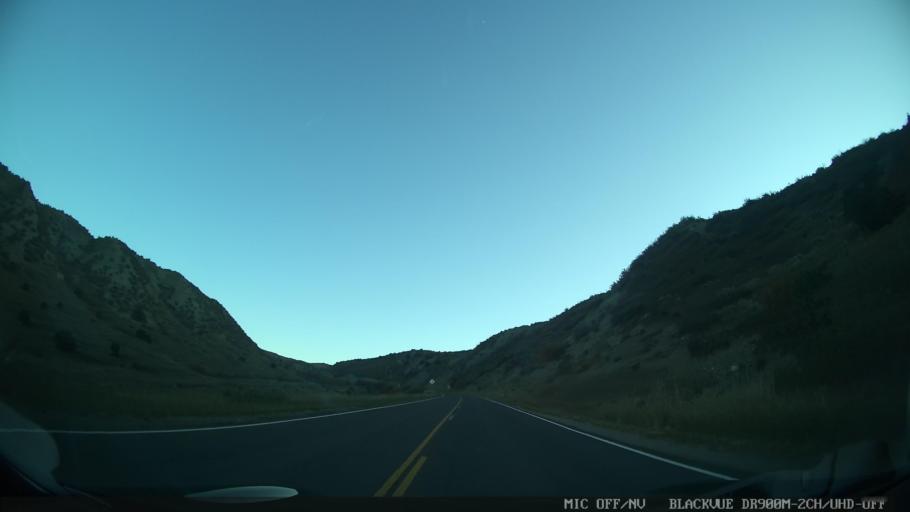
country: US
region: Colorado
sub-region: Eagle County
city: Edwards
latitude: 39.7989
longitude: -106.6795
